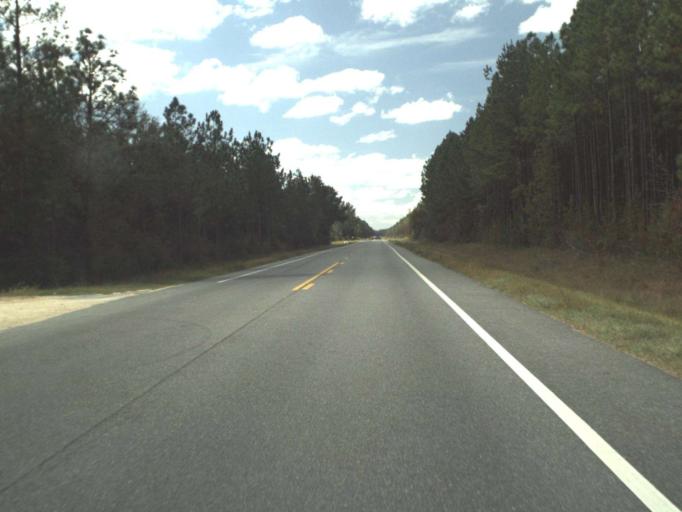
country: US
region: Florida
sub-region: Holmes County
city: Bonifay
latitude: 30.6619
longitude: -85.6505
